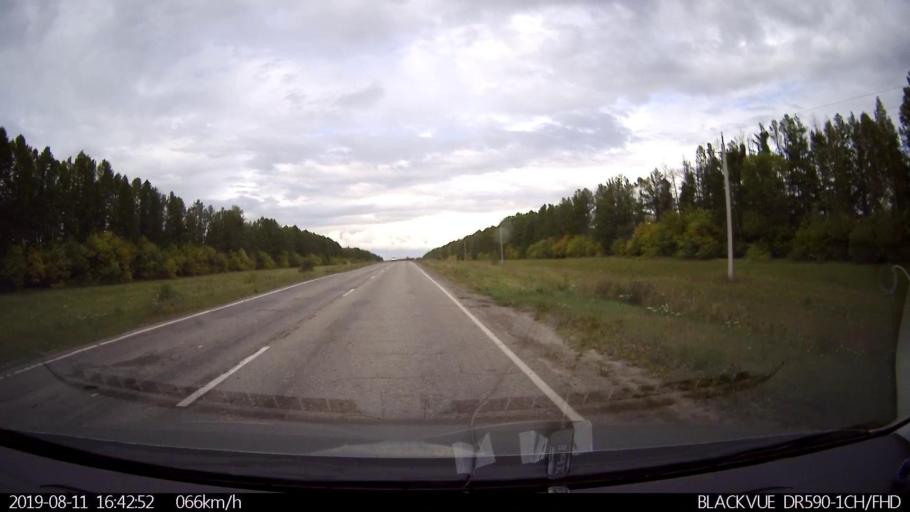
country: RU
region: Ulyanovsk
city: Mayna
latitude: 54.1641
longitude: 47.6665
